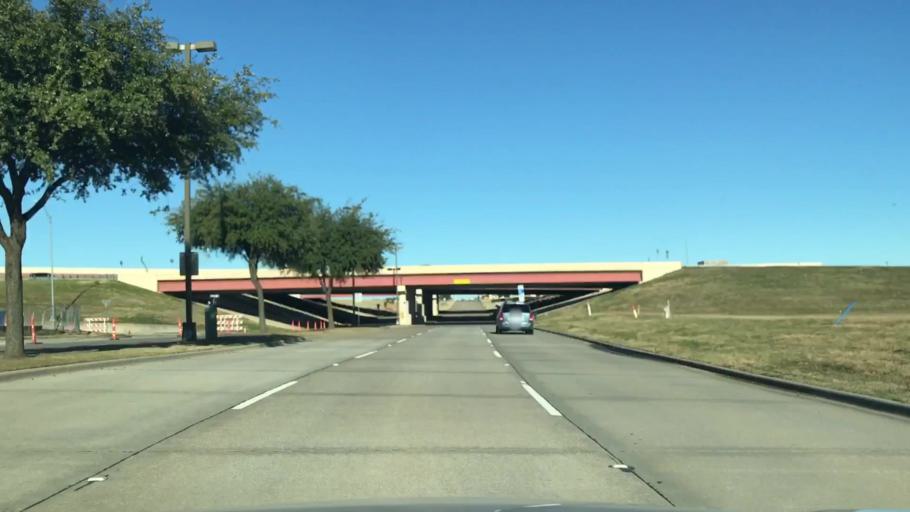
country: US
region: Texas
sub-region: Dallas County
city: Coppell
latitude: 32.8968
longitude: -96.9675
